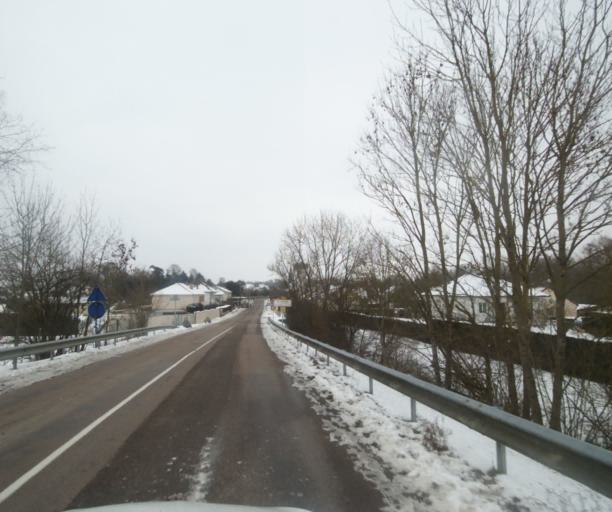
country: FR
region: Champagne-Ardenne
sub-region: Departement de la Haute-Marne
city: Villiers-en-Lieu
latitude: 48.5920
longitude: 4.8602
